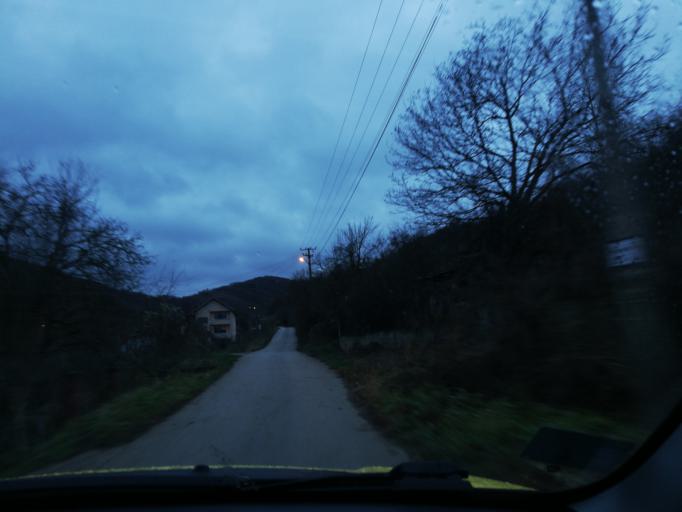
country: RS
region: Central Serbia
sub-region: Pirotski Okrug
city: Dimitrovgrad
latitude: 43.0105
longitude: 22.7202
